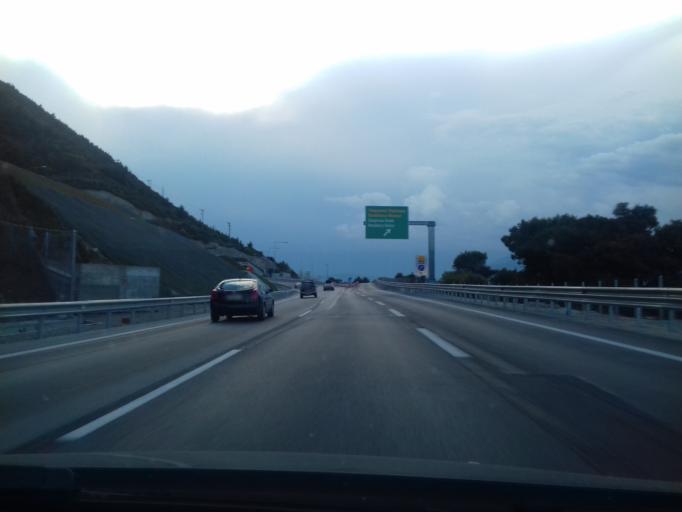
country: GR
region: West Greece
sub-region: Nomos Achaias
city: Kamarai
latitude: 38.3245
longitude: 21.9612
